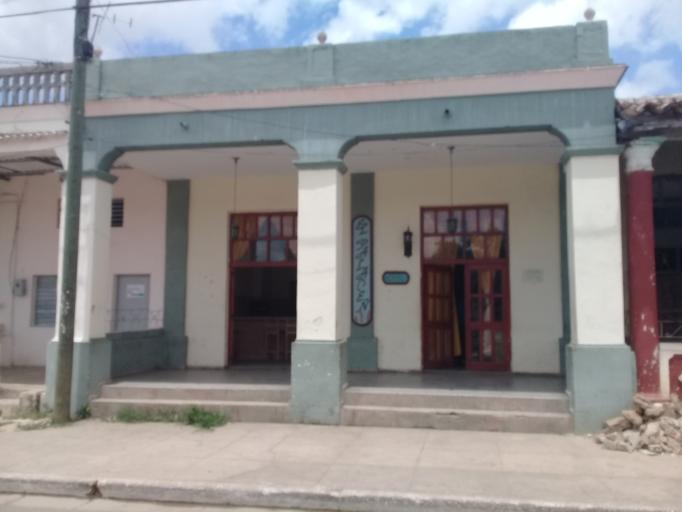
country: CU
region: Pinar del Rio
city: Los Palacios
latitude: 22.5847
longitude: -83.2501
